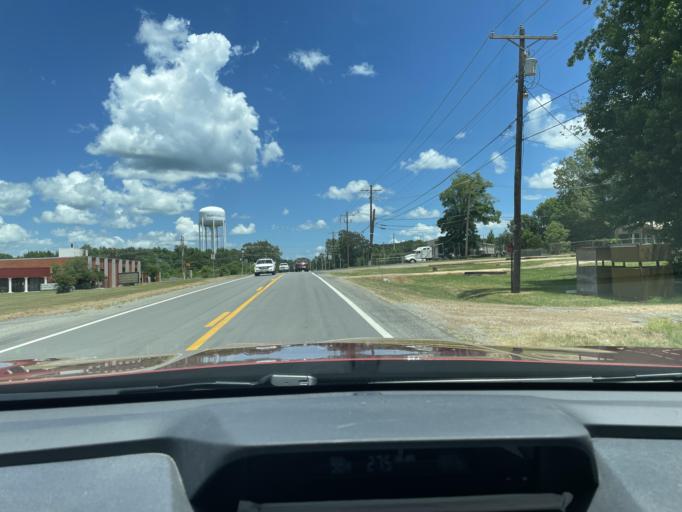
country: US
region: Arkansas
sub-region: Drew County
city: Monticello
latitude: 33.6283
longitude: -91.7706
